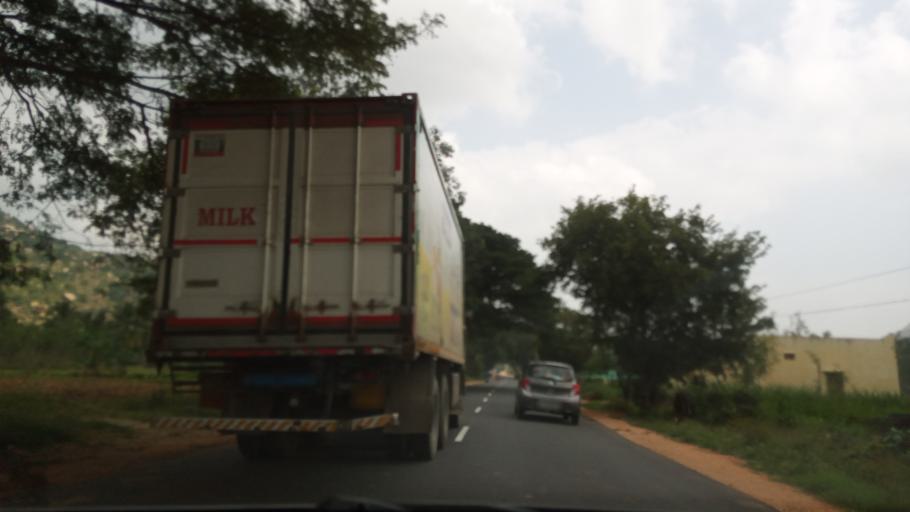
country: IN
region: Andhra Pradesh
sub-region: Chittoor
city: Madanapalle
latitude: 13.6366
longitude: 78.5891
